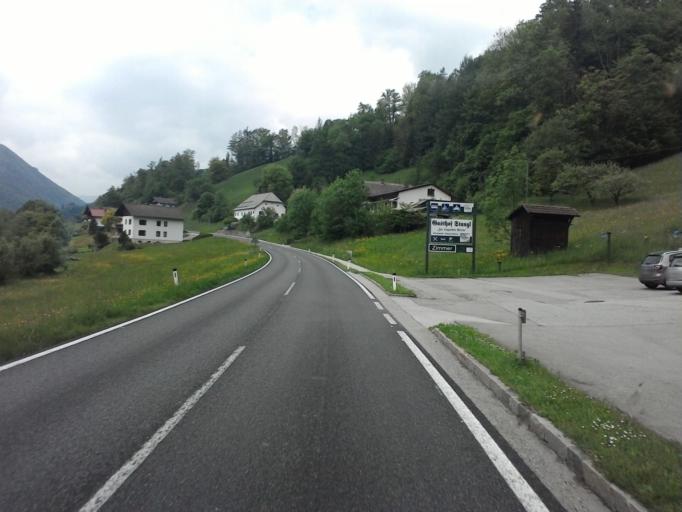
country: AT
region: Upper Austria
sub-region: Politischer Bezirk Steyr-Land
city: Maria Neustift
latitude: 47.8822
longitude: 14.5645
